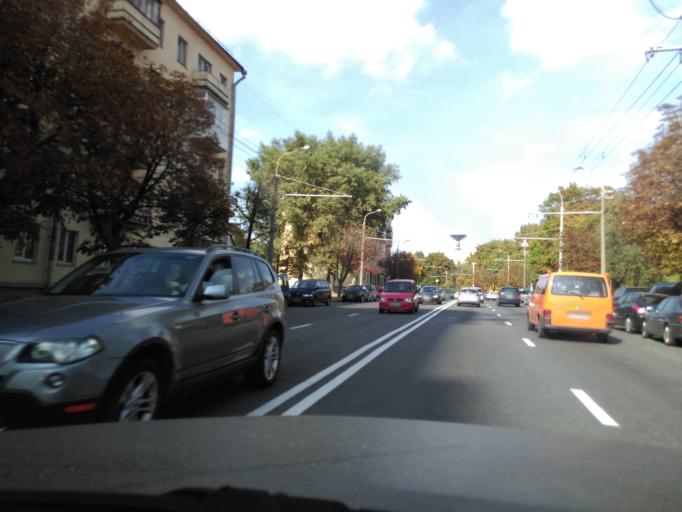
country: BY
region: Minsk
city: Minsk
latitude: 53.9173
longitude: 27.6038
